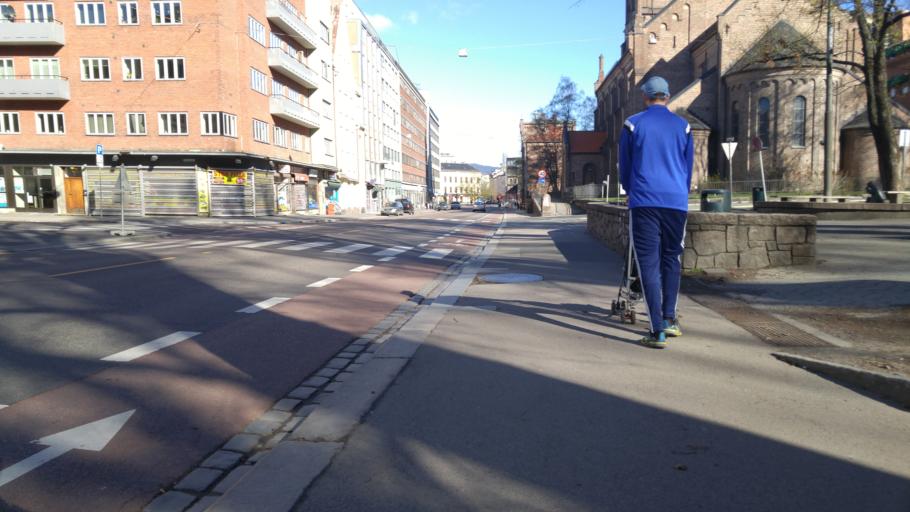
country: NO
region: Oslo
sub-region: Oslo
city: Oslo
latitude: 59.9103
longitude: 10.7679
